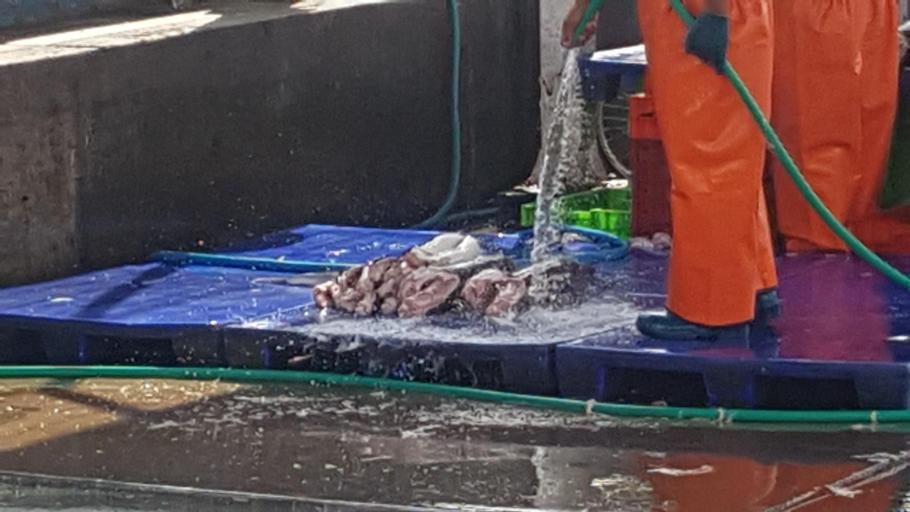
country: PE
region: Moquegua
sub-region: Provincia de Ilo
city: Ilo
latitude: -17.6436
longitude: -71.3442
